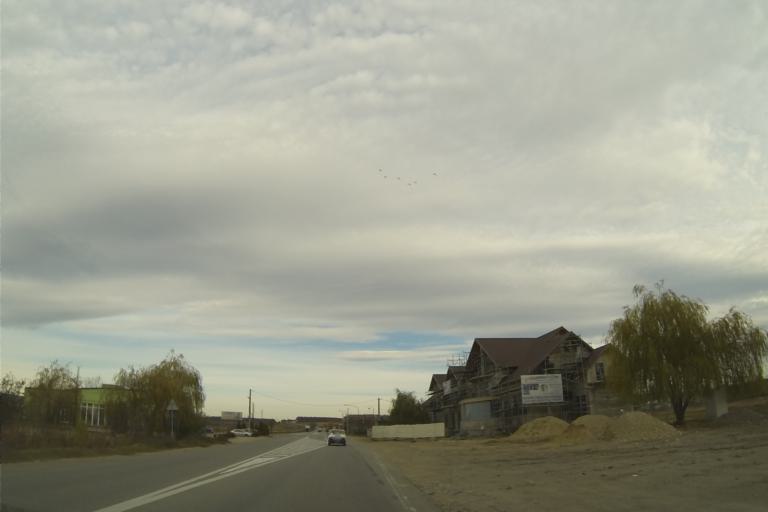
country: RO
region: Olt
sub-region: Comuna Scornicesti
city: Scornicesti
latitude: 44.5508
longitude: 24.5572
